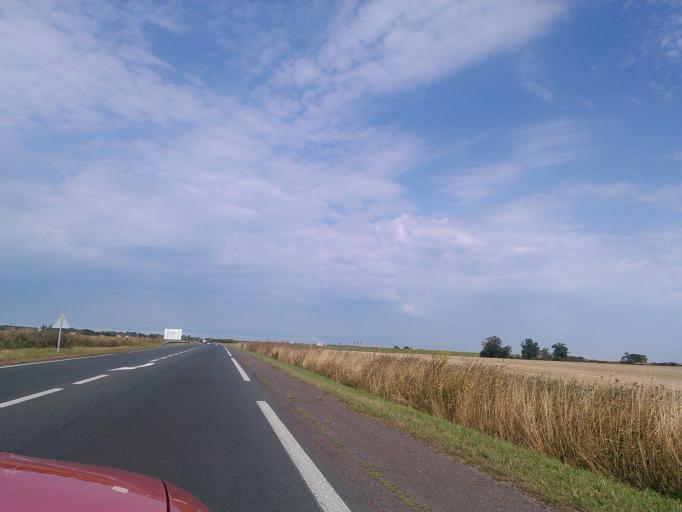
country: FR
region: Poitou-Charentes
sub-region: Departement de la Charente-Maritime
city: Etaules
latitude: 45.7420
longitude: -1.0936
